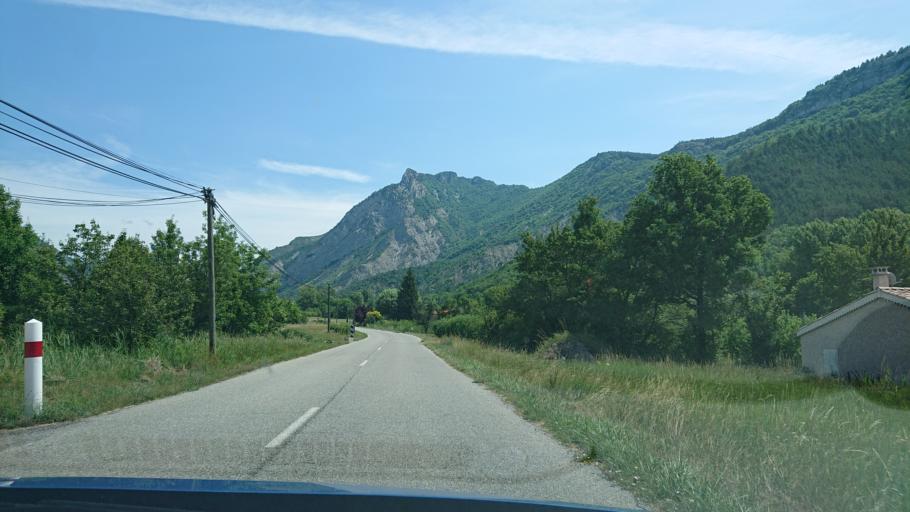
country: FR
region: Provence-Alpes-Cote d'Azur
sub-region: Departement des Hautes-Alpes
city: Tallard
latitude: 44.3466
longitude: 6.0340
